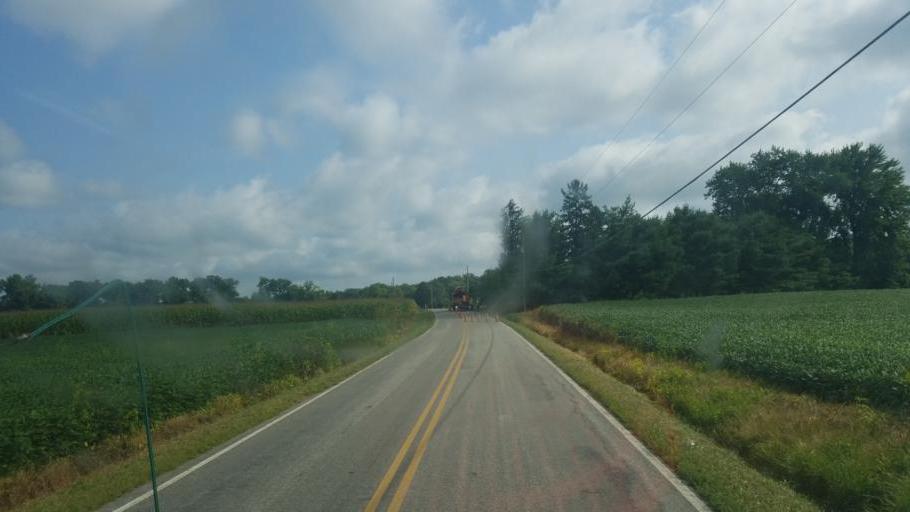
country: US
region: Ohio
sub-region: Morrow County
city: Cardington
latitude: 40.5641
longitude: -82.9973
